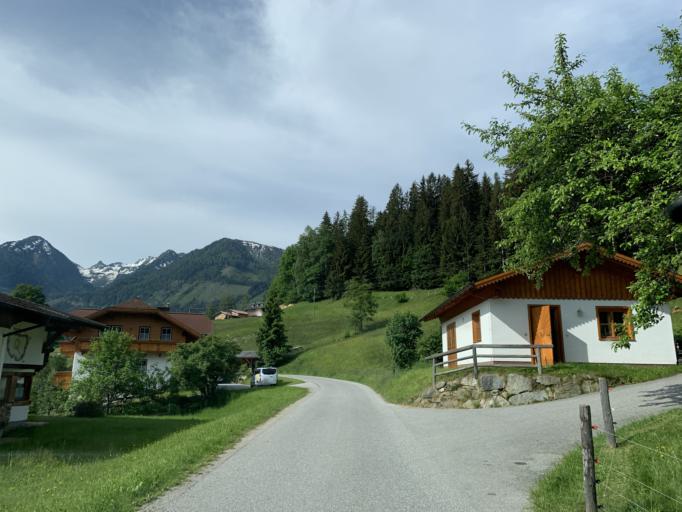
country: AT
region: Styria
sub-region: Politischer Bezirk Liezen
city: Schladming
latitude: 47.3697
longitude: 13.6667
